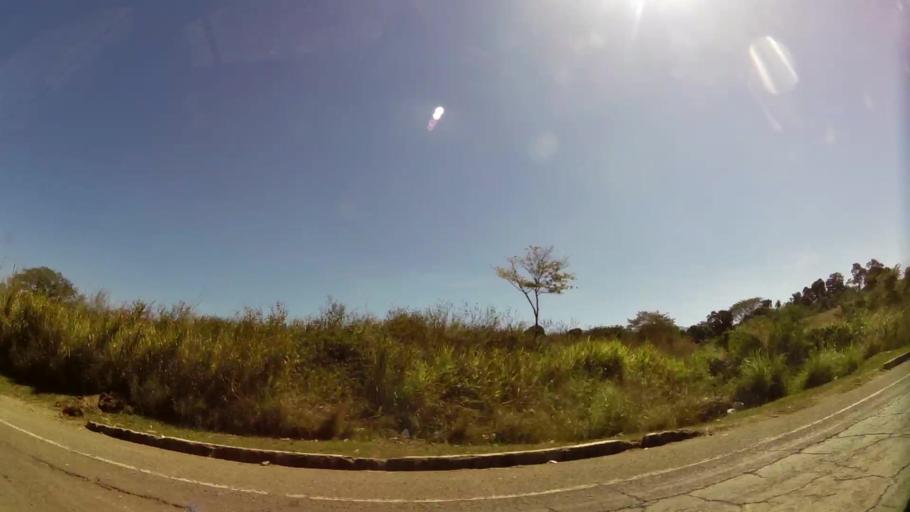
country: SV
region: Ahuachapan
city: Ahuachapan
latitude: 13.9419
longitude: -89.8425
